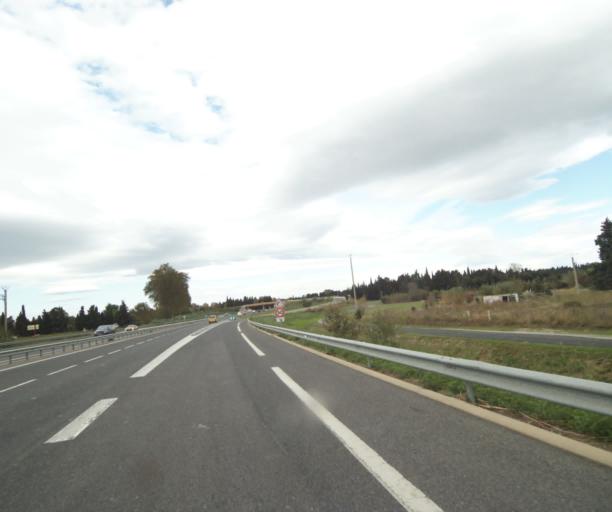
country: FR
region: Languedoc-Roussillon
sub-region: Departement des Pyrenees-Orientales
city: Elne
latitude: 42.5871
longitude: 2.9838
